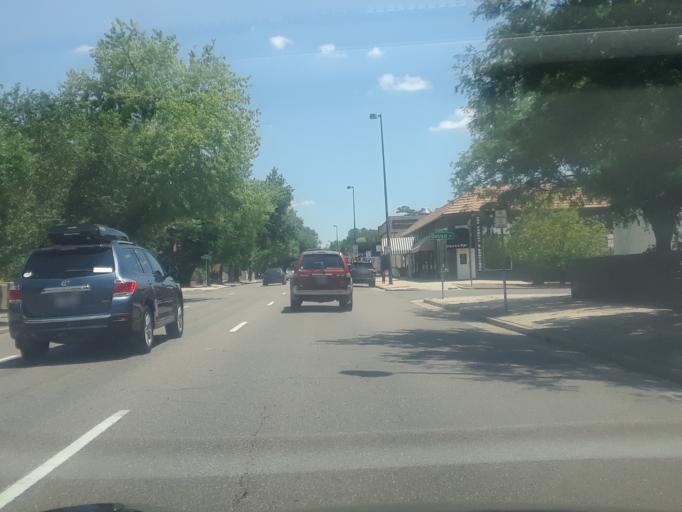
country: US
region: Colorado
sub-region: Arapahoe County
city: Glendale
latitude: 39.7256
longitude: -104.9552
